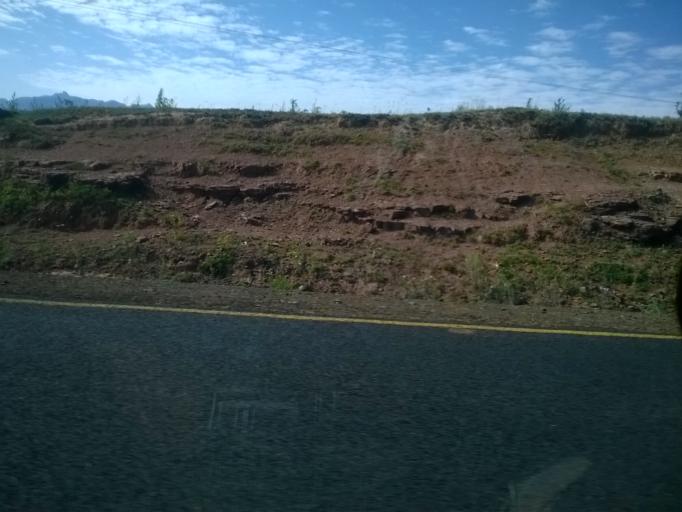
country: LS
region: Berea
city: Teyateyaneng
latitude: -29.0915
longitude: 27.9385
